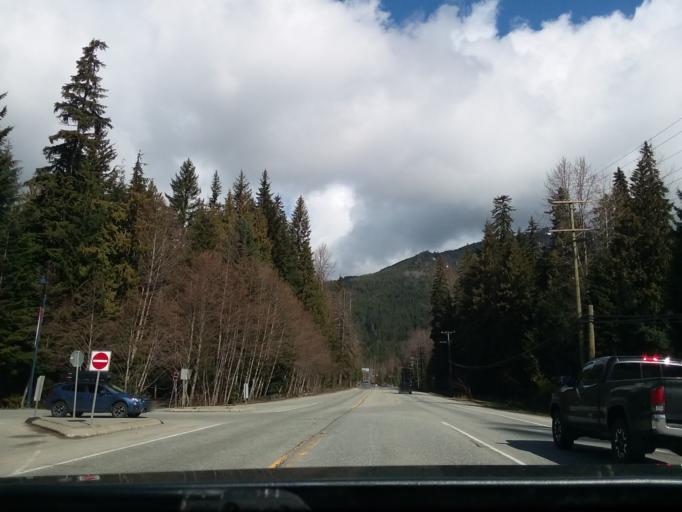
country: CA
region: British Columbia
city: Whistler
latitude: 50.1455
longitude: -122.9593
